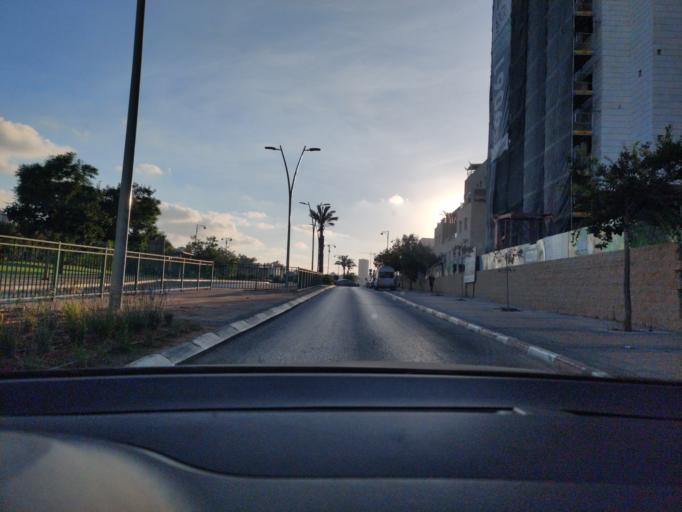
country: IL
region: Central District
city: Elyakhin
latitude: 32.4324
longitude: 34.9438
